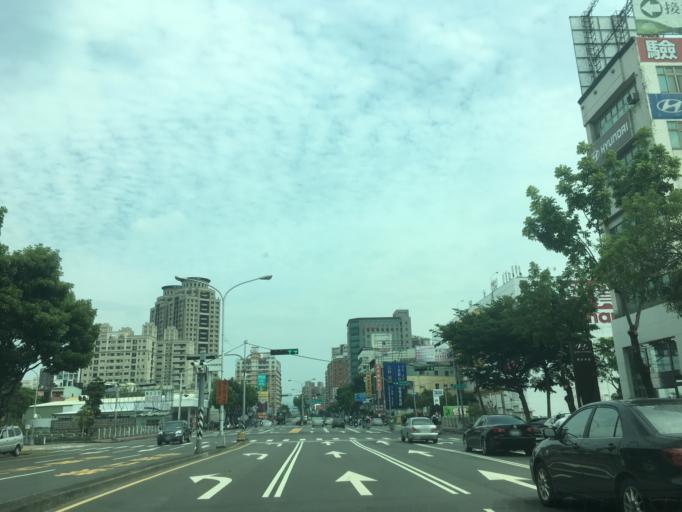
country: TW
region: Taiwan
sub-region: Taichung City
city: Taichung
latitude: 24.1172
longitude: 120.6534
